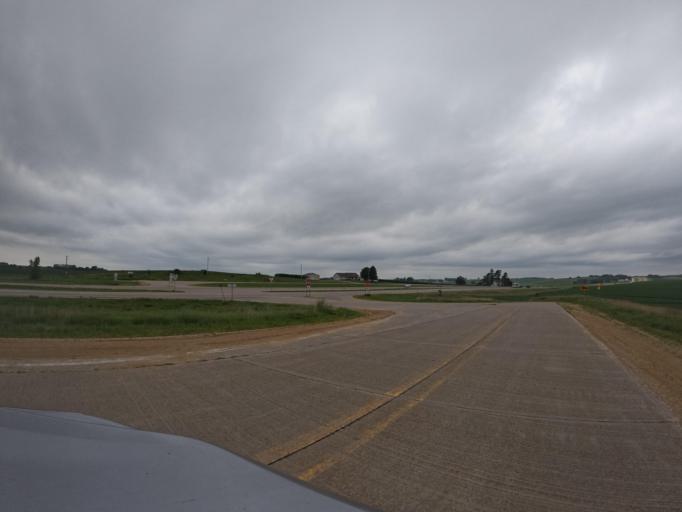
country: US
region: Iowa
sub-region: Jackson County
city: Maquoketa
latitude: 41.9499
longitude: -90.6318
